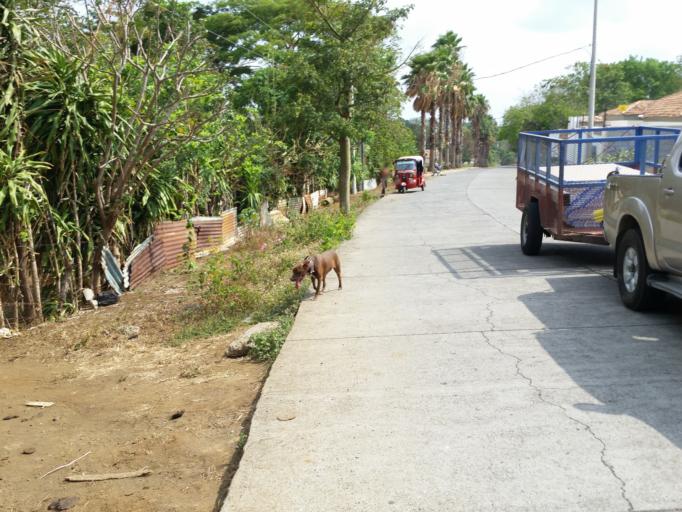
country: NI
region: Masaya
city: Ticuantepe
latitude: 12.0679
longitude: -86.2487
